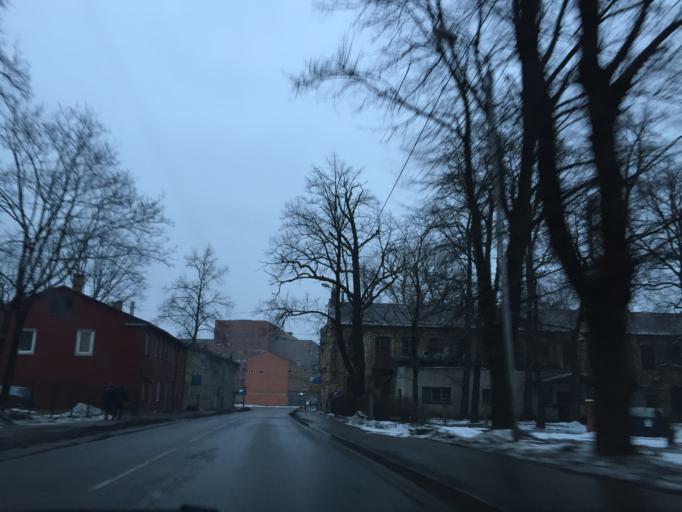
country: LV
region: Riga
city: Riga
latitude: 56.9638
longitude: 24.0709
